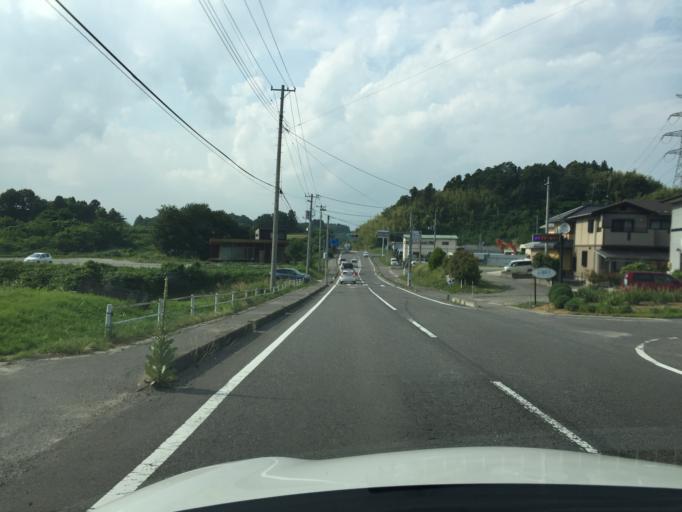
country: JP
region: Fukushima
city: Miharu
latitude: 37.4264
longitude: 140.4471
